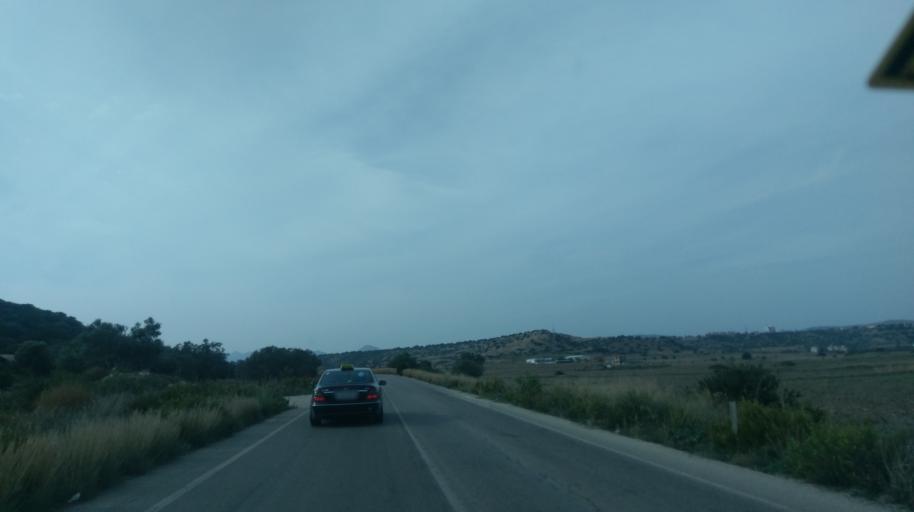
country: CY
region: Ammochostos
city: Leonarisso
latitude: 35.4020
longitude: 34.0848
